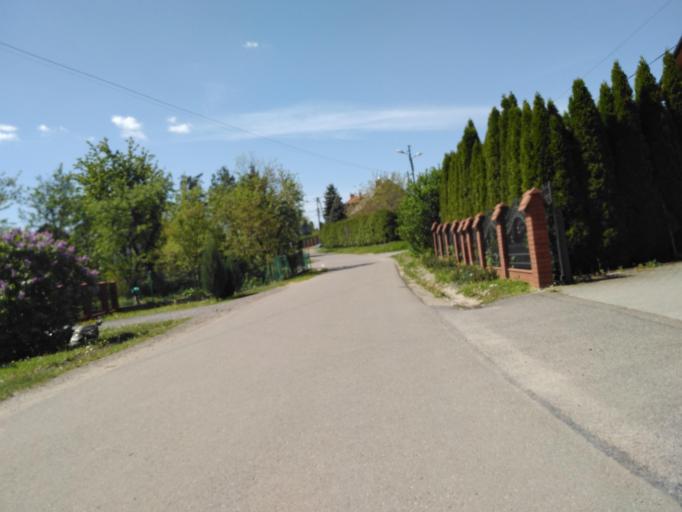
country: PL
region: Subcarpathian Voivodeship
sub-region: Powiat krosnienski
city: Miejsce Piastowe
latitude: 49.6195
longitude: 21.7638
